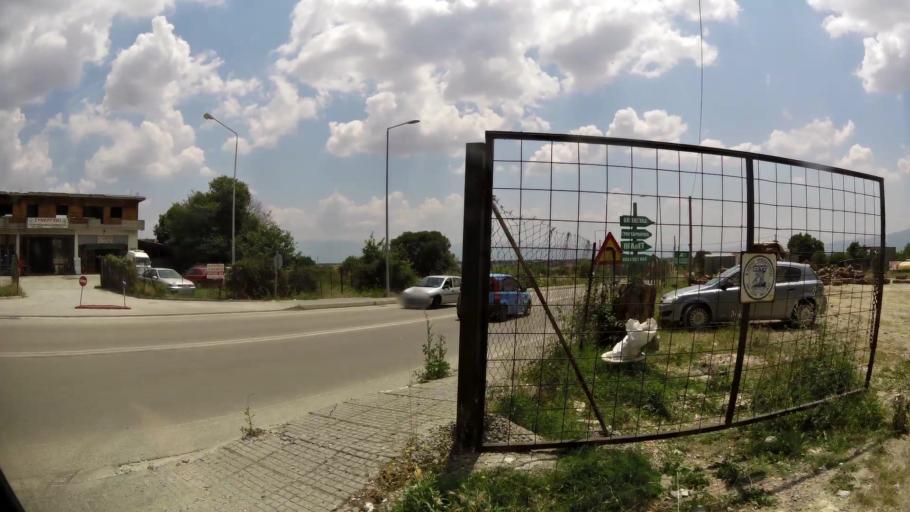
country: GR
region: West Macedonia
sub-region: Nomos Kozanis
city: Kozani
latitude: 40.2873
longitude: 21.7984
